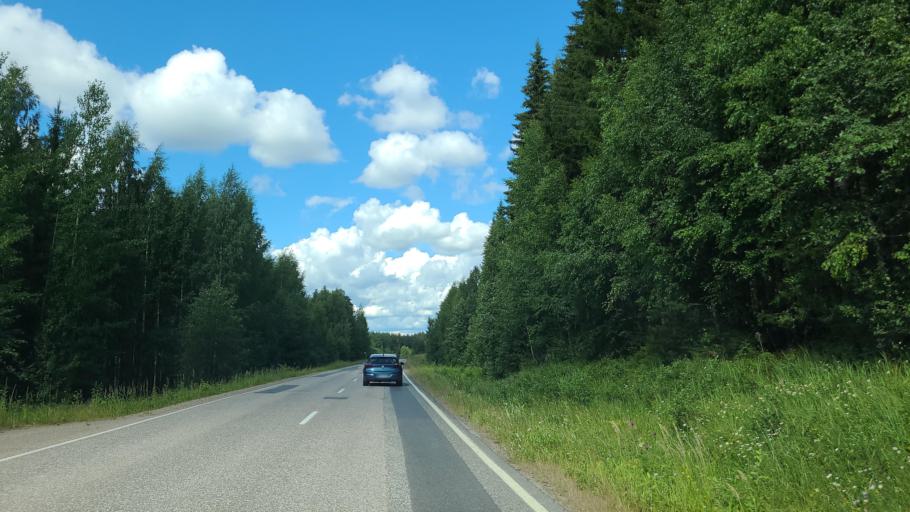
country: FI
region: Northern Savo
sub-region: Koillis-Savo
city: Kaavi
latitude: 62.9081
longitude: 28.7167
